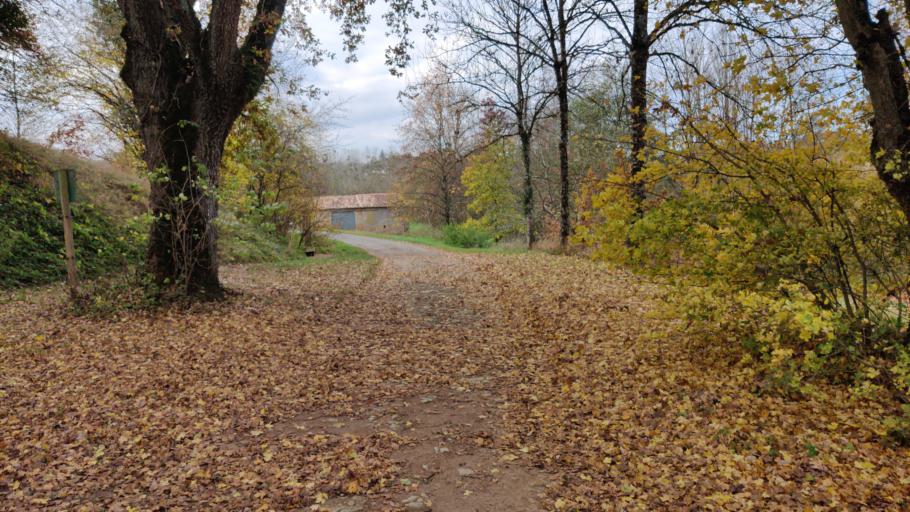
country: FR
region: Poitou-Charentes
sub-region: Departement de la Vienne
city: Rouille
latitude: 46.4651
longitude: 0.0726
